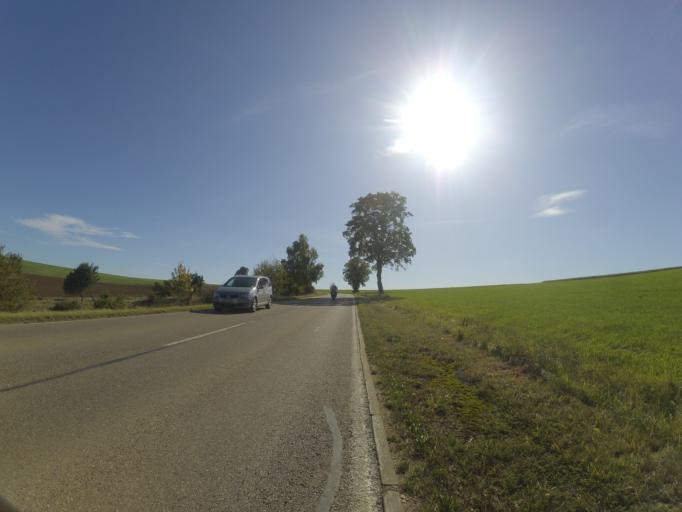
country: DE
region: Baden-Wuerttemberg
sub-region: Tuebingen Region
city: Borslingen
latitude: 48.5453
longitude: 10.0526
